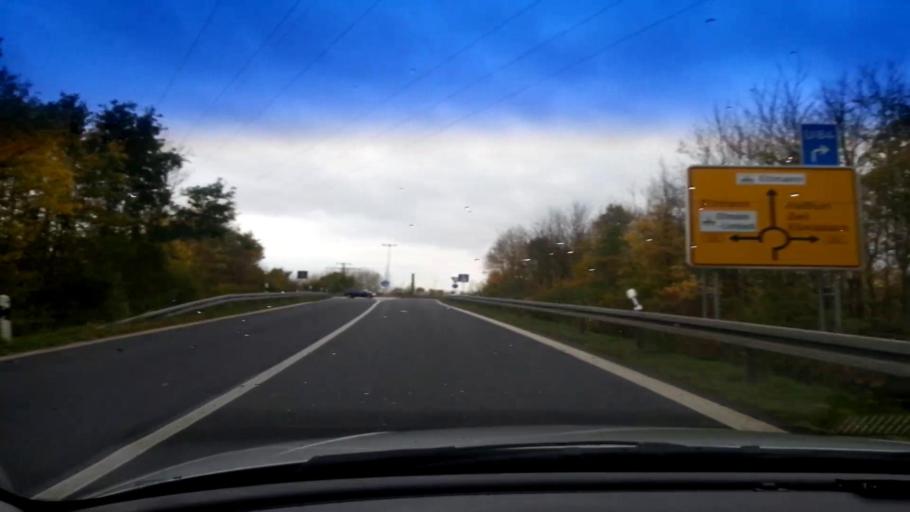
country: DE
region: Bavaria
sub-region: Regierungsbezirk Unterfranken
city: Ebelsbach
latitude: 49.9789
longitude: 10.6732
